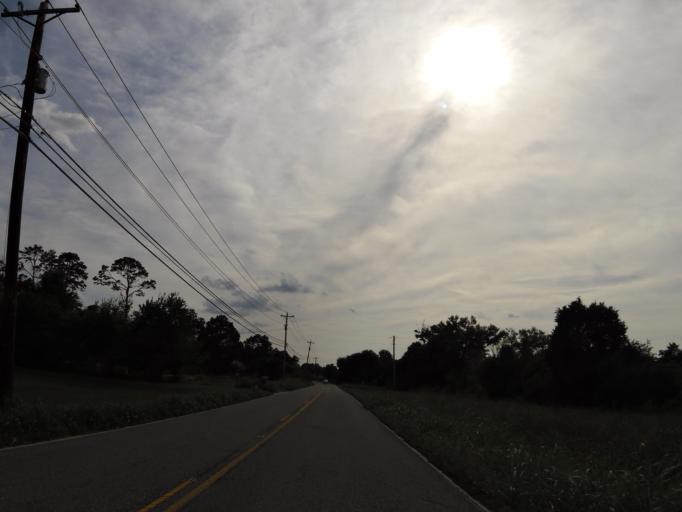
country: US
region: Tennessee
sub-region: Blount County
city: Wildwood
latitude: 35.8217
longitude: -83.8187
